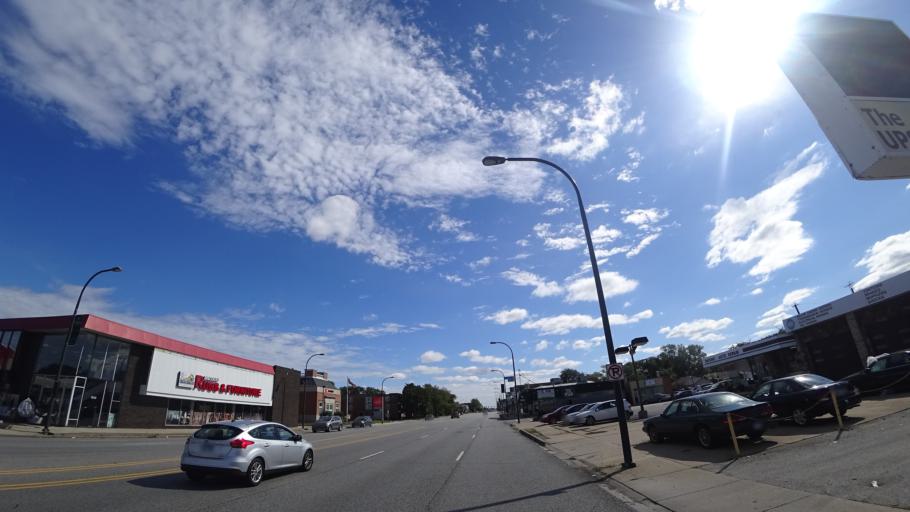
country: US
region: Illinois
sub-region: Cook County
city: Oak Lawn
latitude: 41.7170
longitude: -87.7408
